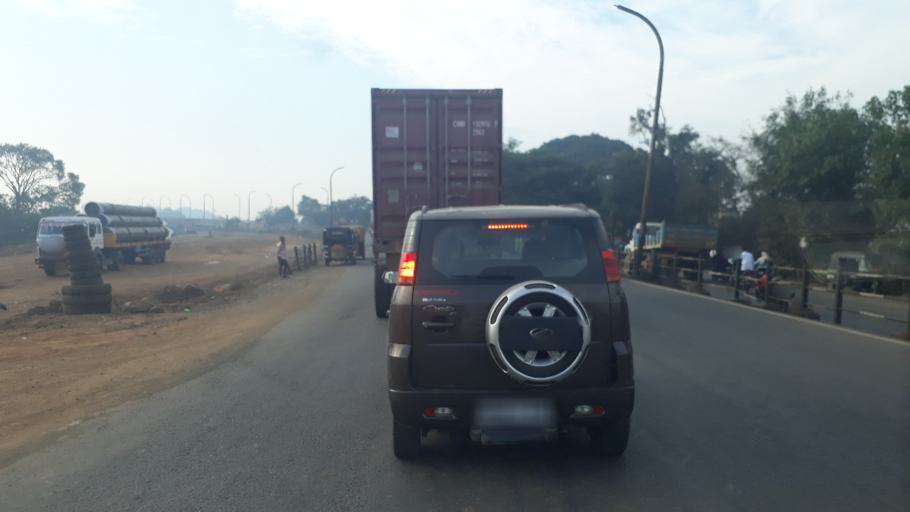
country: IN
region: Maharashtra
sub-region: Raigarh
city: Pen
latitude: 18.8429
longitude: 73.0934
